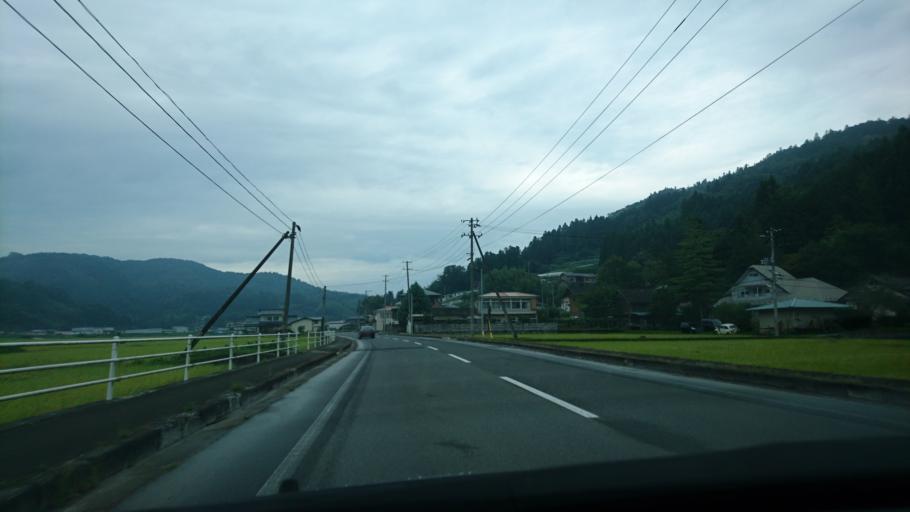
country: JP
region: Iwate
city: Ichinoseki
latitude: 38.9720
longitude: 141.2440
